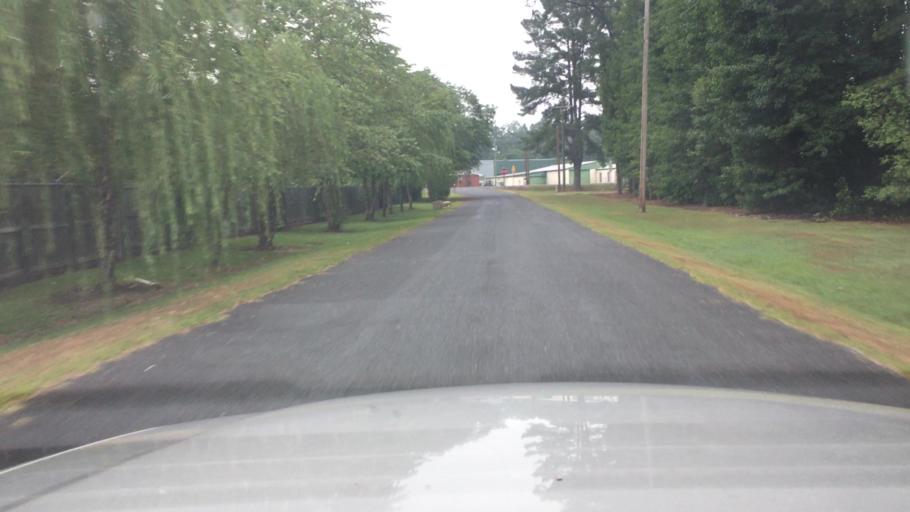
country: US
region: North Carolina
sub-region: Cumberland County
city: Fayetteville
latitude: 34.9985
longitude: -78.8577
